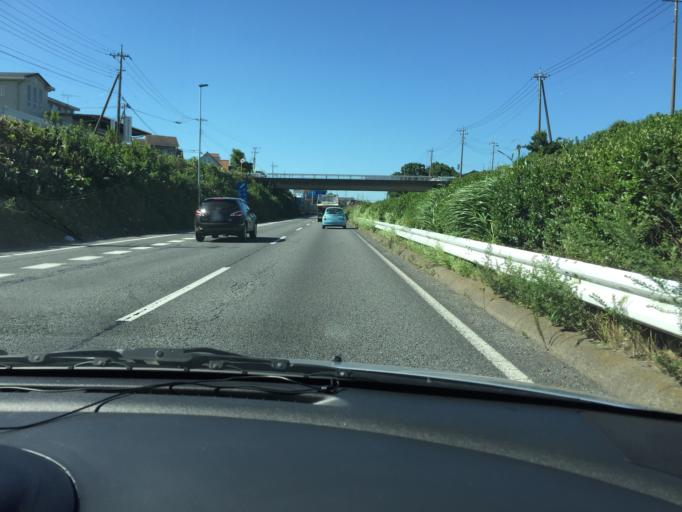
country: JP
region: Ibaraki
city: Naka
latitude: 36.0651
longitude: 140.1791
